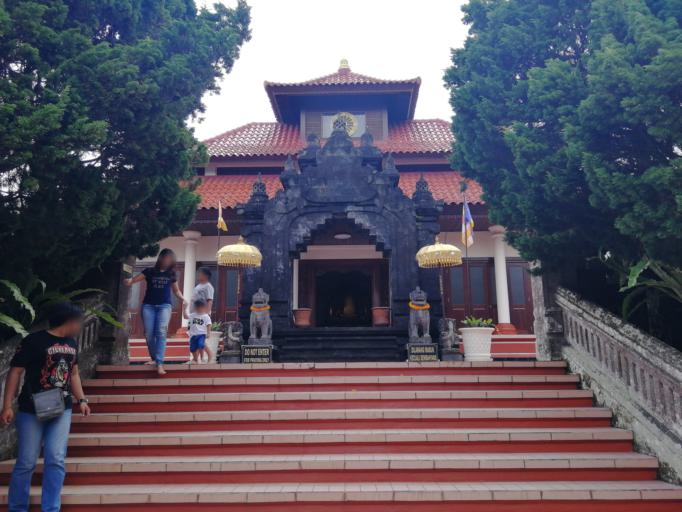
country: ID
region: Bali
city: Bantiran
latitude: -8.3194
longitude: 115.0177
